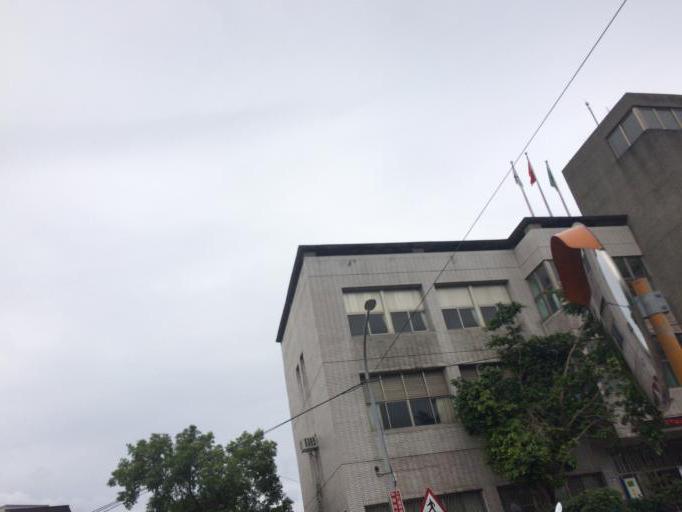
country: TW
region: Taiwan
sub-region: Hualien
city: Hualian
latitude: 23.9785
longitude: 121.6138
